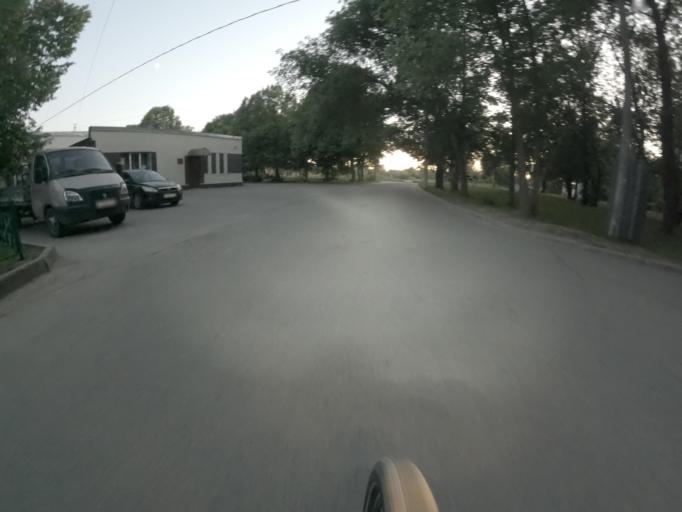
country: RU
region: St.-Petersburg
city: Sapernyy
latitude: 59.7778
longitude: 30.6921
